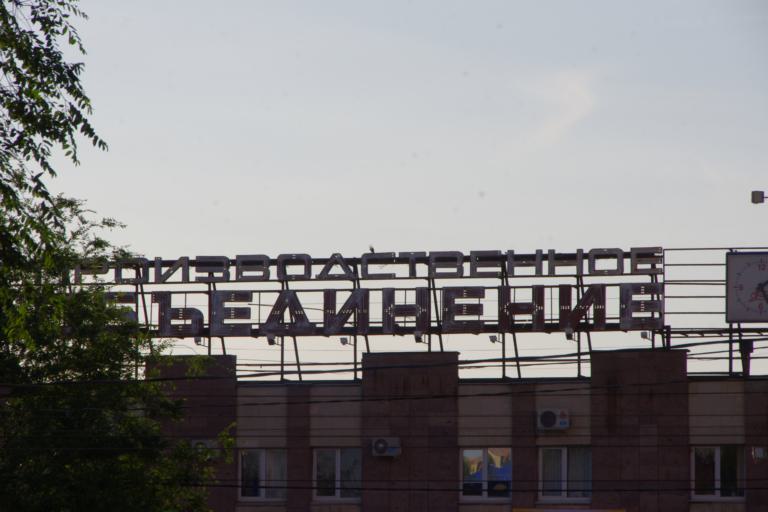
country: RU
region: Samara
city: Samara
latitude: 53.2162
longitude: 50.1491
